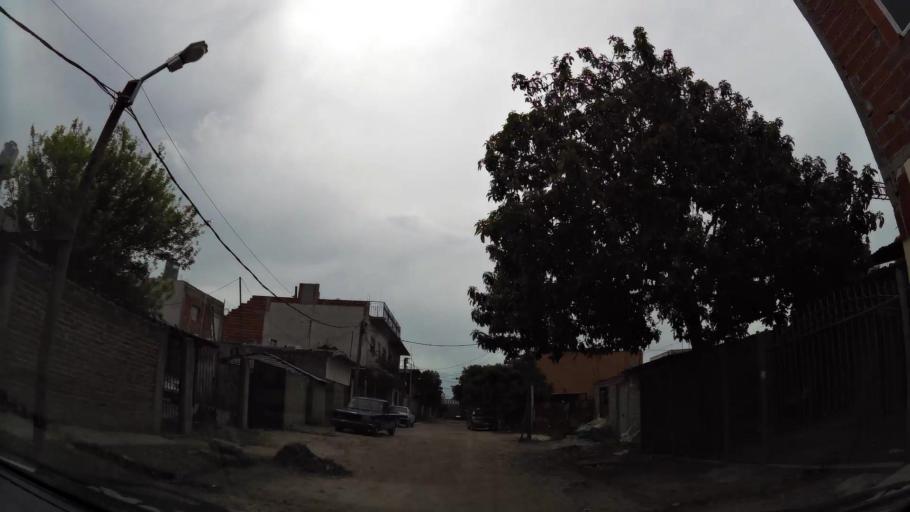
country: AR
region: Buenos Aires
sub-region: Partido de Quilmes
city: Quilmes
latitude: -34.7571
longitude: -58.2559
